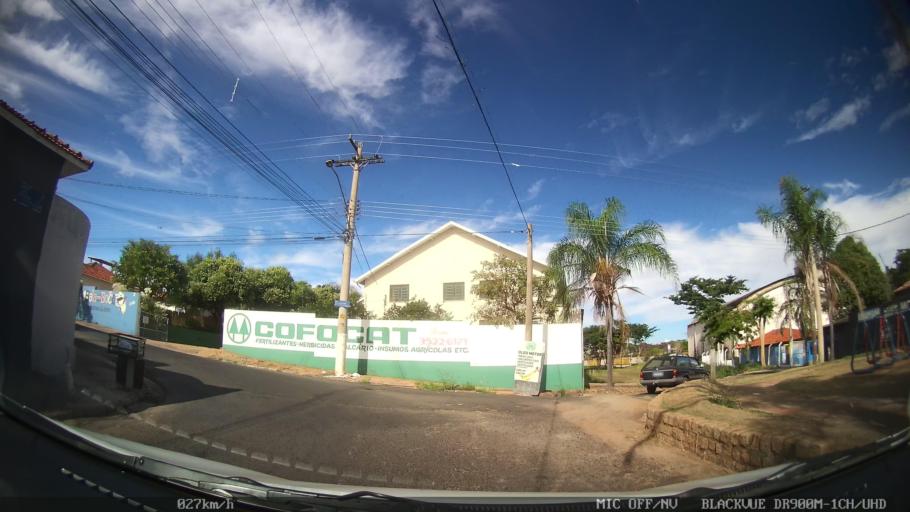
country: BR
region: Sao Paulo
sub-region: Catanduva
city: Catanduva
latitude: -21.1255
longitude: -48.9771
